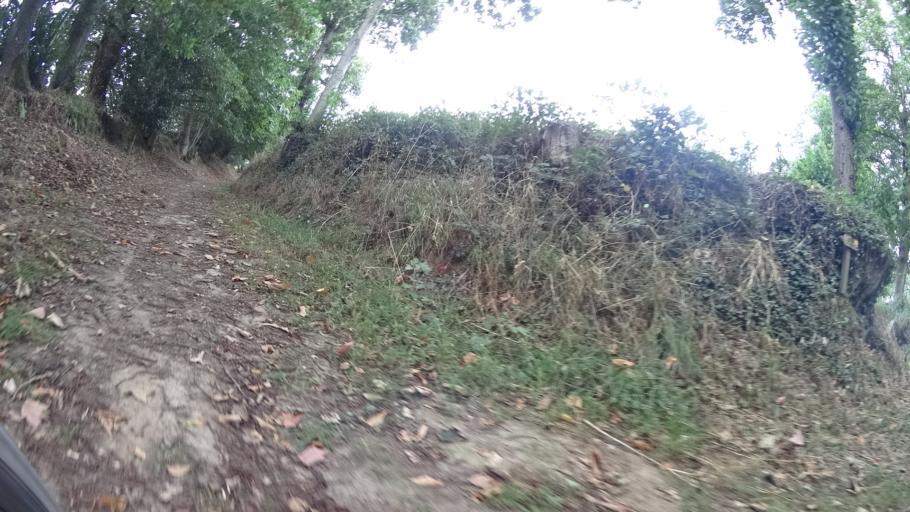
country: FR
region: Brittany
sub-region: Departement d'Ille-et-Vilaine
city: Geveze
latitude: 48.2304
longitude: -1.7815
